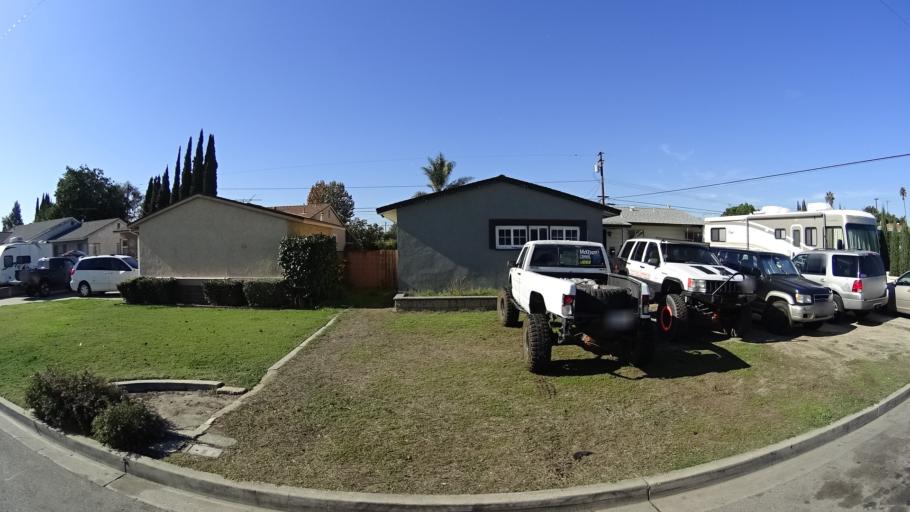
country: US
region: California
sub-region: Orange County
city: Garden Grove
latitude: 33.7835
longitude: -117.9305
